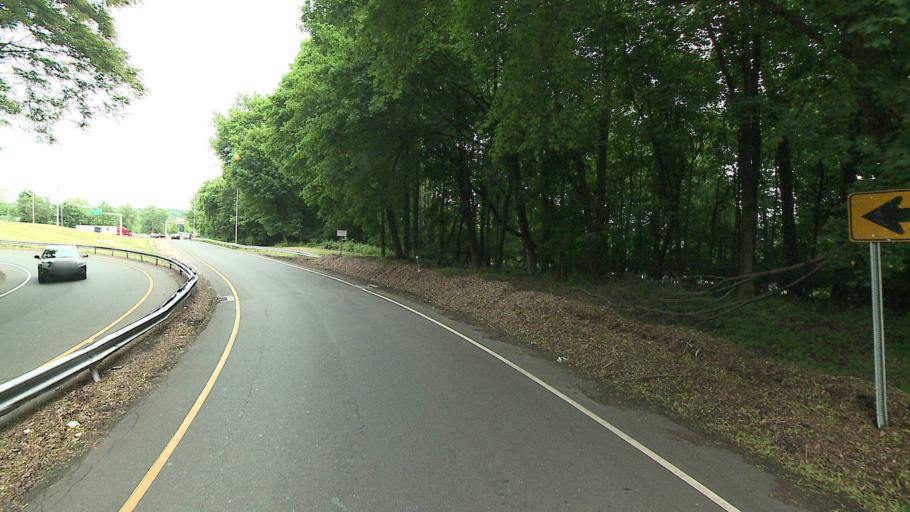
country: US
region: Connecticut
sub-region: Fairfield County
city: Riverside
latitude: 41.0401
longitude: -73.5762
